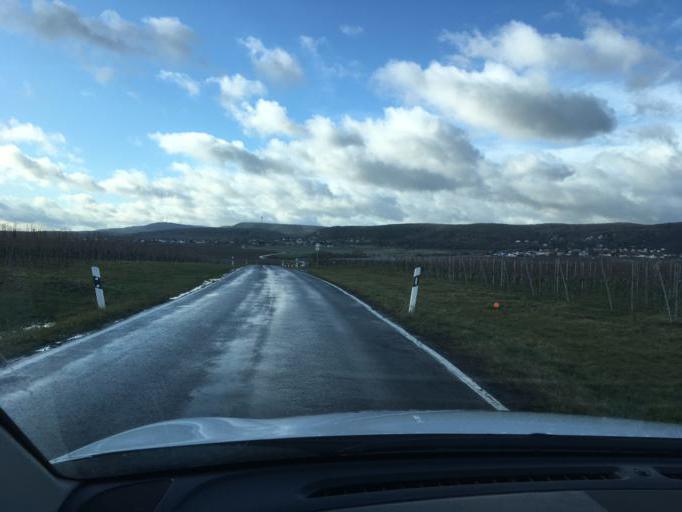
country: DE
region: Rheinland-Pfalz
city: Kirchheim an der Weinstrasse
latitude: 49.5302
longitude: 8.1721
